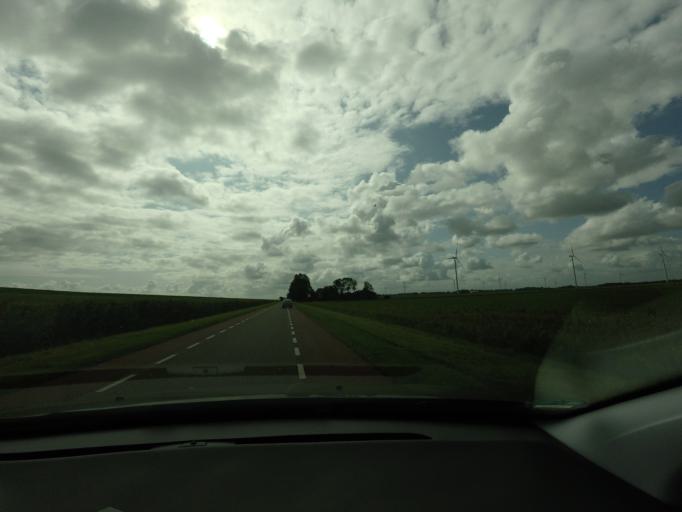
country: NL
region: North Holland
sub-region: Gemeente Medemblik
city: Medemblik
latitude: 52.8375
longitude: 5.1114
